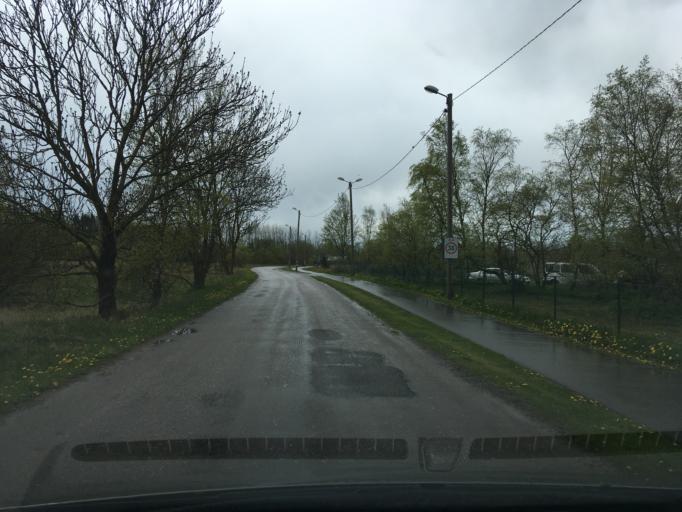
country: EE
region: Harju
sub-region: Joelaehtme vald
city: Loo
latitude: 59.4359
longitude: 24.9582
